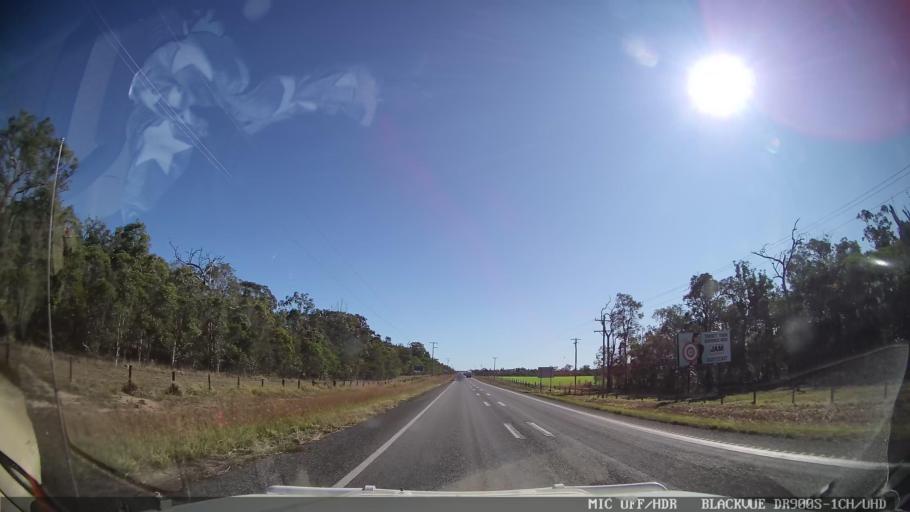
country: AU
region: Queensland
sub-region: Bundaberg
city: Childers
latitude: -25.2510
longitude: 152.3536
